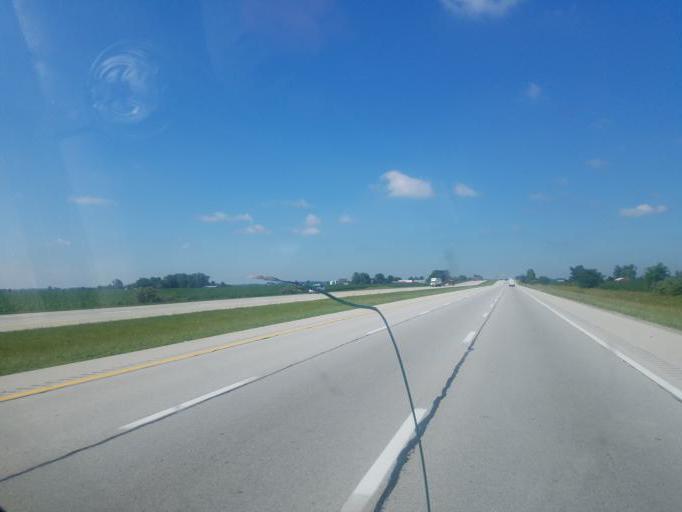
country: US
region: Ohio
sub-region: Greene County
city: Jamestown
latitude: 39.5964
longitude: -83.6511
